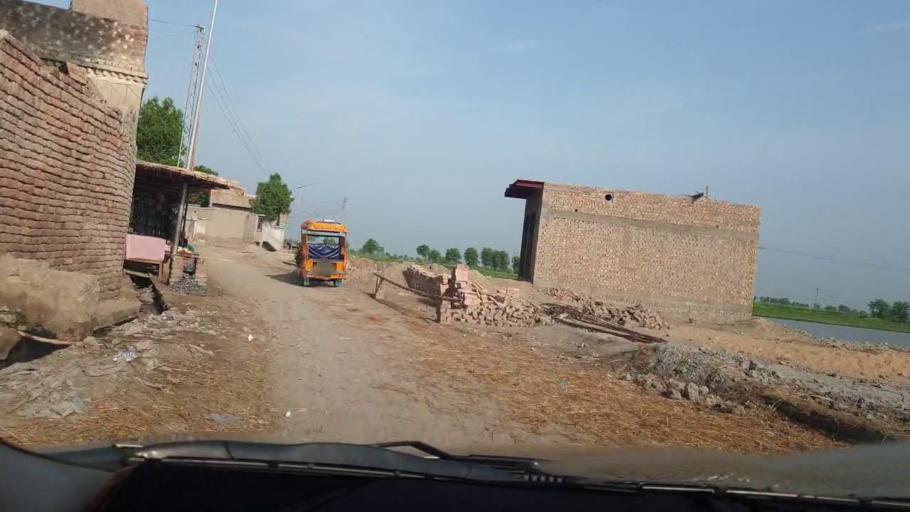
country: PK
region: Sindh
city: Goth Garelo
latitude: 27.4812
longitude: 68.0864
